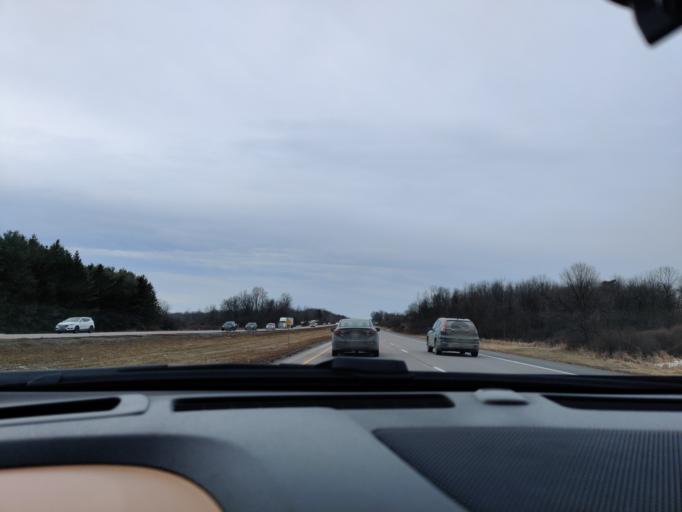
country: CA
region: Ontario
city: Gananoque
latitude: 44.3494
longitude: -76.1118
